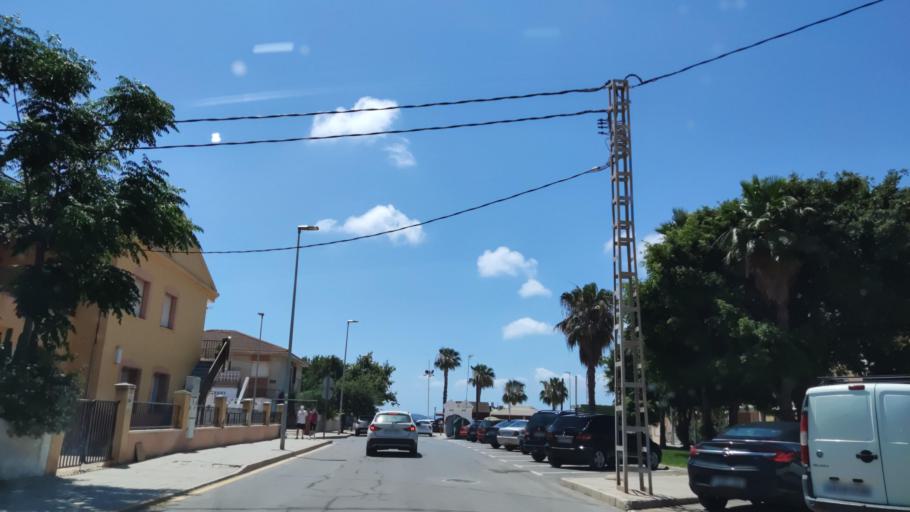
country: ES
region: Murcia
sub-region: Murcia
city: Los Alcazares
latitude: 37.7541
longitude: -0.8375
